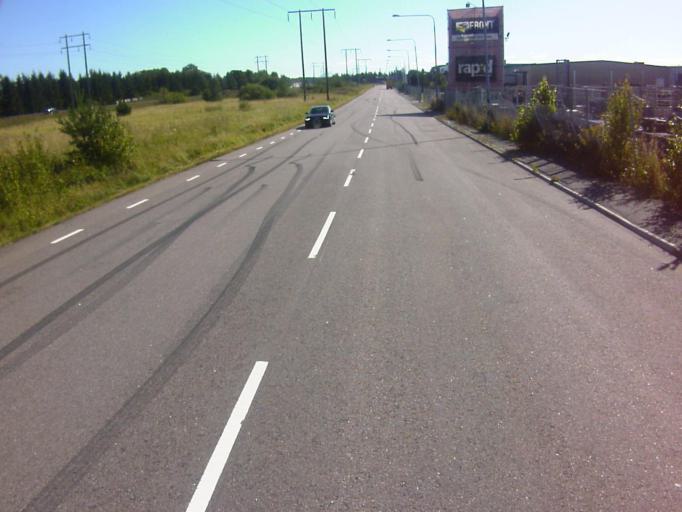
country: SE
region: Soedermanland
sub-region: Eskilstuna Kommun
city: Torshalla
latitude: 59.3891
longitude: 16.4809
